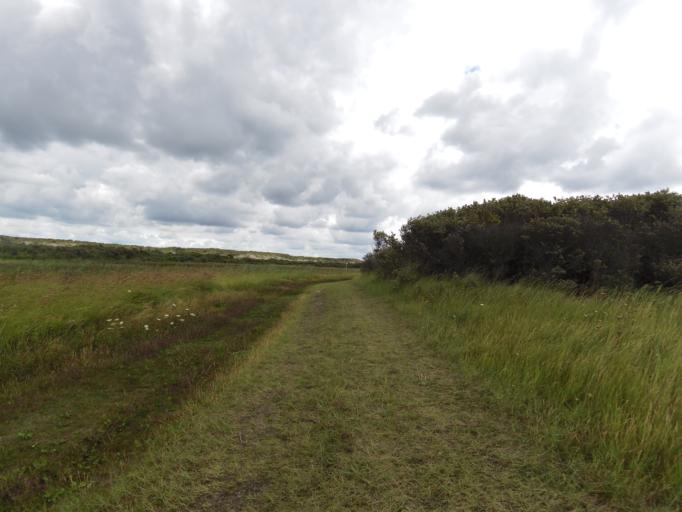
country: NL
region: South Holland
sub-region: Gemeente Goeree-Overflakkee
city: Goedereede
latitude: 51.8401
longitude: 3.9774
